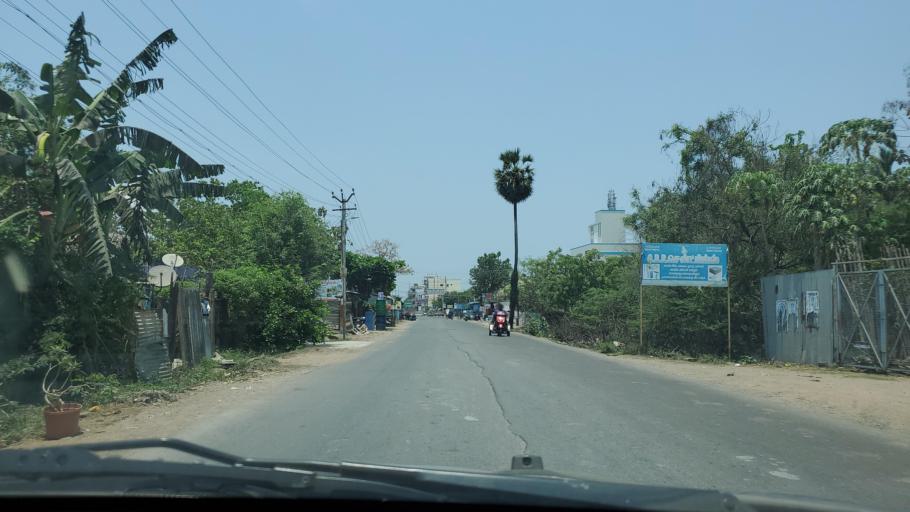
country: IN
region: Tamil Nadu
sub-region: Kancheepuram
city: Vengavasal
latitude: 12.8553
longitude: 80.1718
